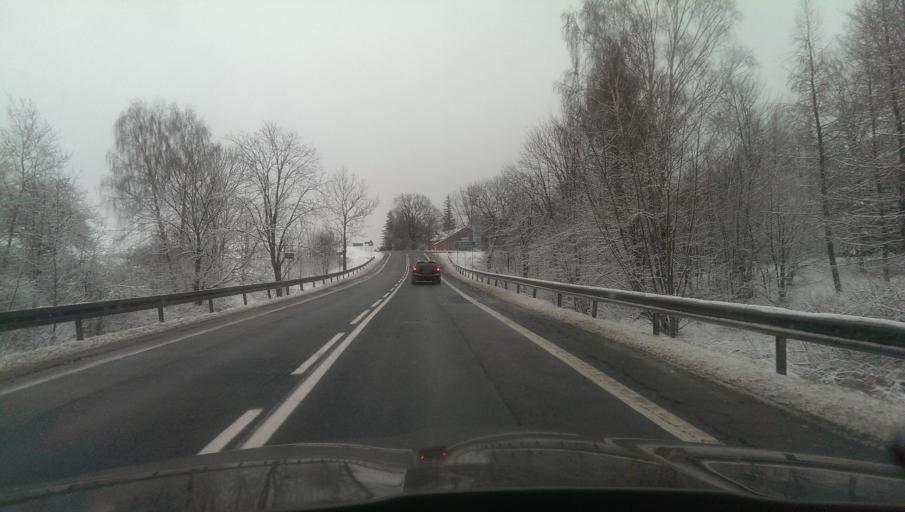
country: PL
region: Subcarpathian Voivodeship
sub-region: Powiat krosnienski
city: Sieniawa
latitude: 49.5807
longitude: 21.9225
